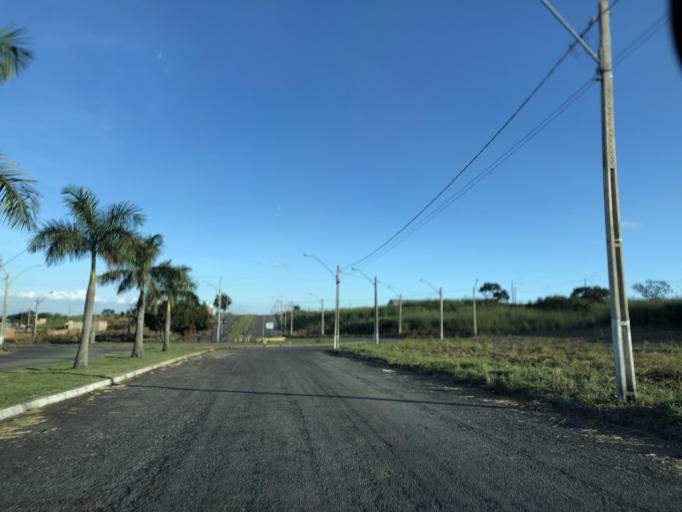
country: BR
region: Goias
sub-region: Luziania
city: Luziania
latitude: -16.2665
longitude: -47.9713
